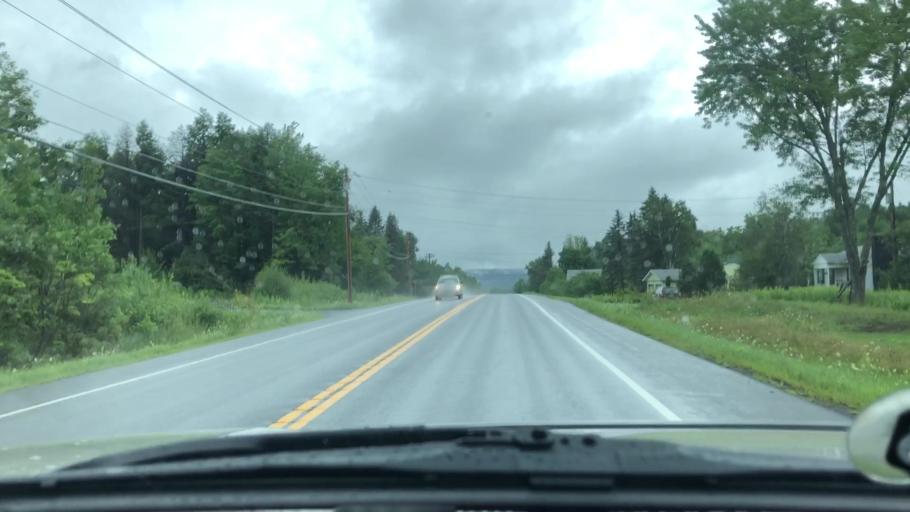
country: US
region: New York
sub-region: Greene County
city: Cairo
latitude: 42.3032
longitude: -74.2094
